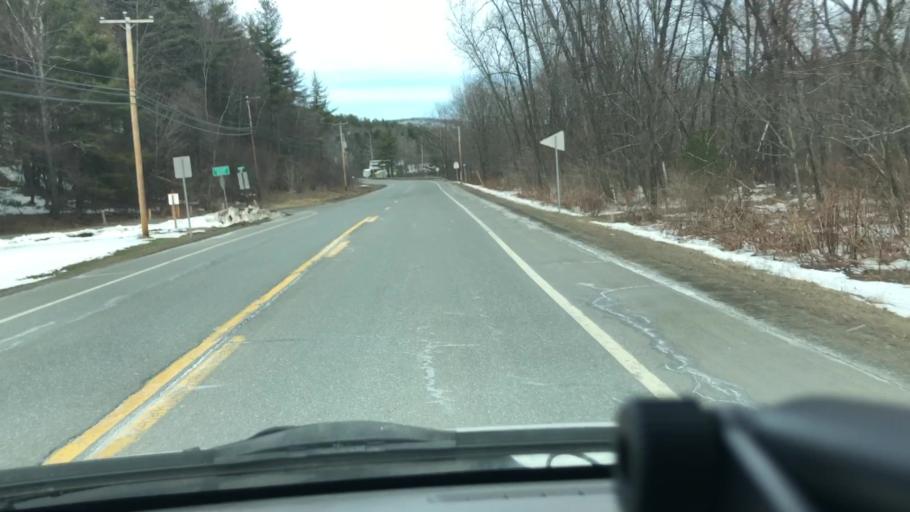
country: US
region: Massachusetts
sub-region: Franklin County
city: Buckland
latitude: 42.5944
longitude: -72.7855
